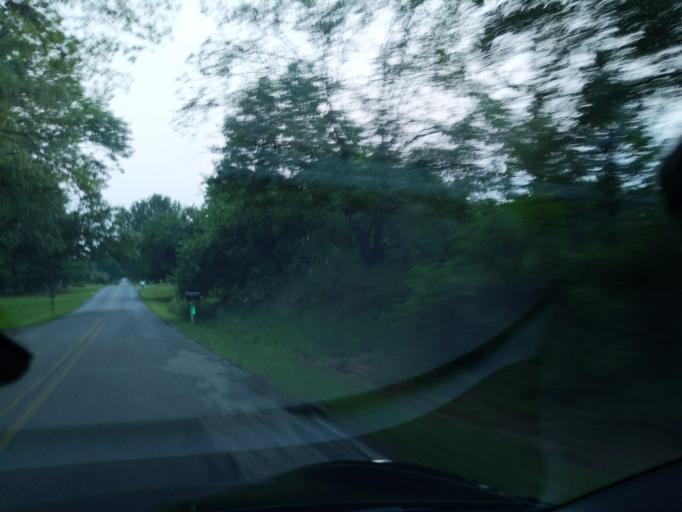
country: US
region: Michigan
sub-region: Ingham County
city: Leslie
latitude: 42.3714
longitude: -84.4948
